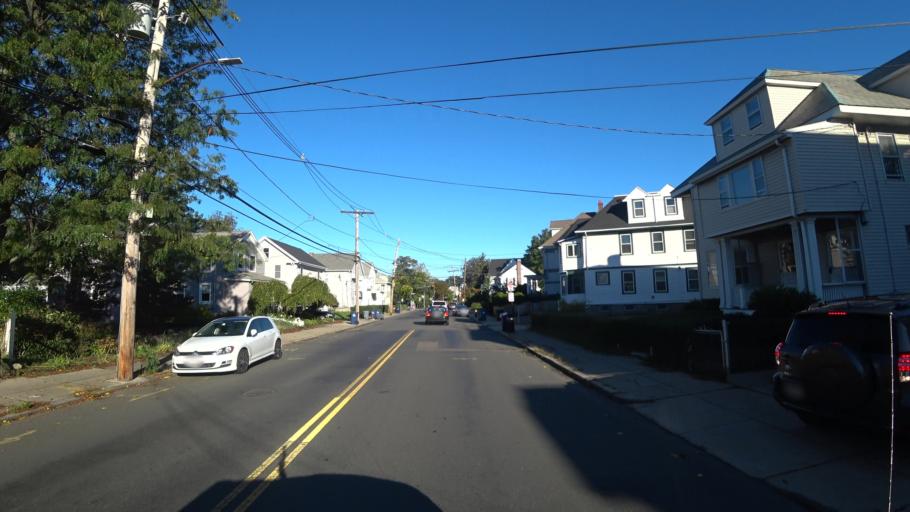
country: US
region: Massachusetts
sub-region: Middlesex County
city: Watertown
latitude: 42.3545
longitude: -71.1552
